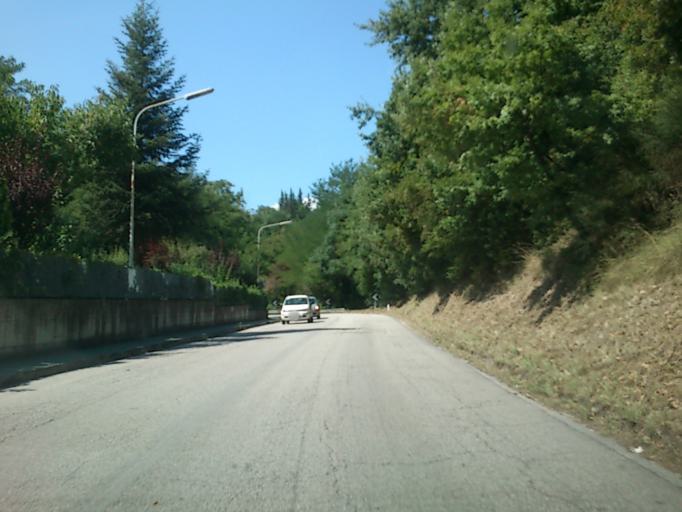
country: IT
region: The Marches
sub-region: Provincia di Pesaro e Urbino
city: Tavernelle
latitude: 43.7370
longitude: 12.8920
